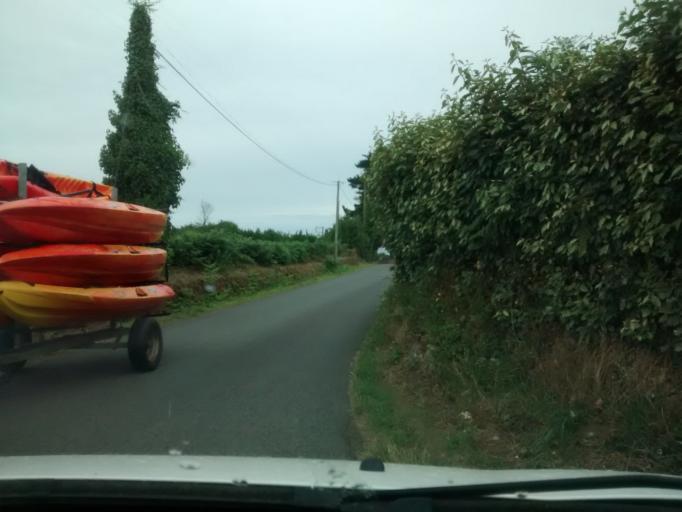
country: FR
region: Brittany
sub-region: Departement des Cotes-d'Armor
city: Penvenan
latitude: 48.8328
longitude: -3.3085
